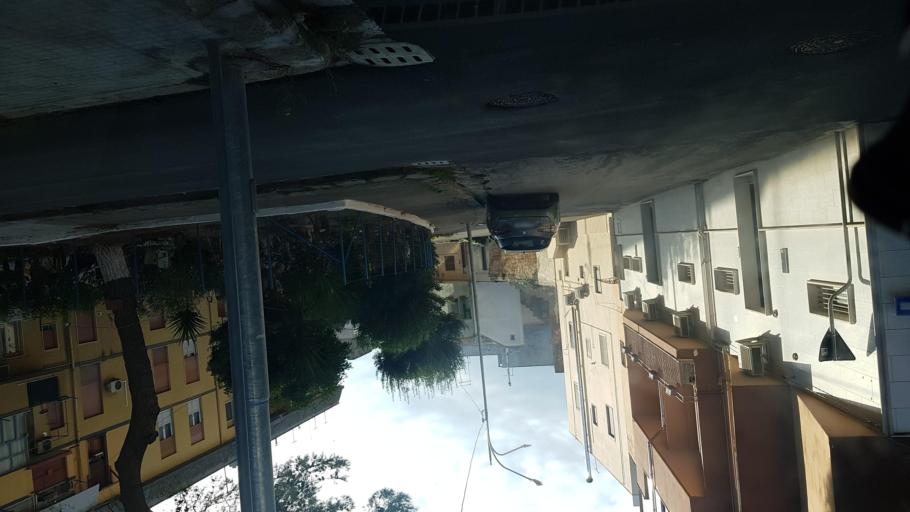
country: IT
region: Apulia
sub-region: Provincia di Brindisi
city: Francavilla Fontana
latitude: 40.5341
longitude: 17.5855
